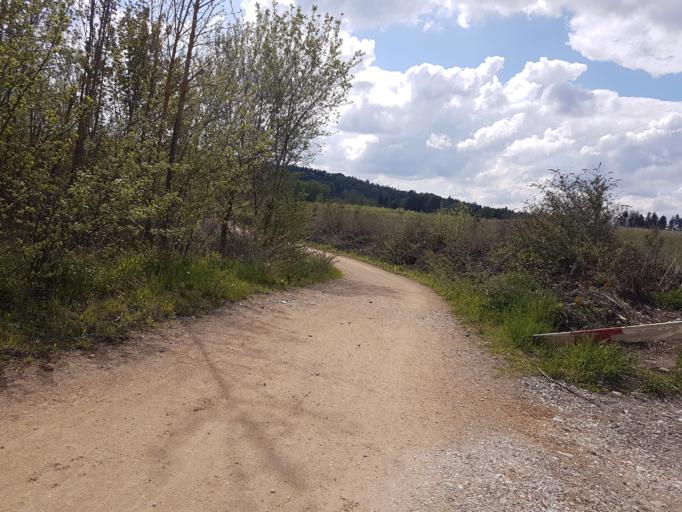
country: CH
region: Solothurn
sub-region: Bezirk Olten
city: Gunzgen
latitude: 47.2972
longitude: 7.8454
